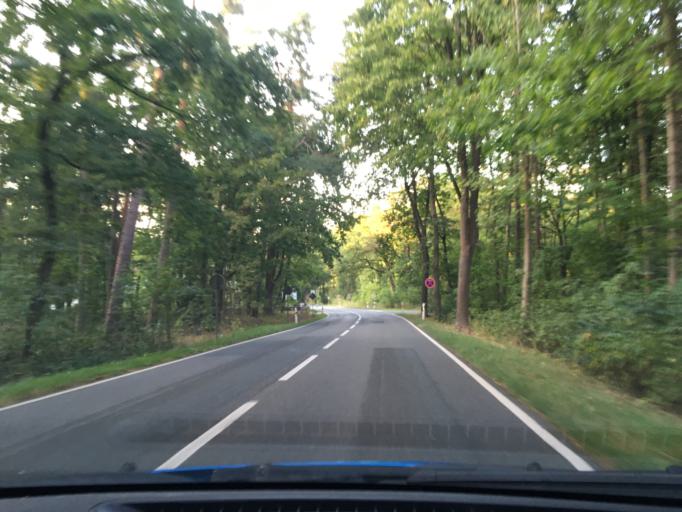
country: DE
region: Lower Saxony
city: Bleckede
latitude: 53.2708
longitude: 10.7438
